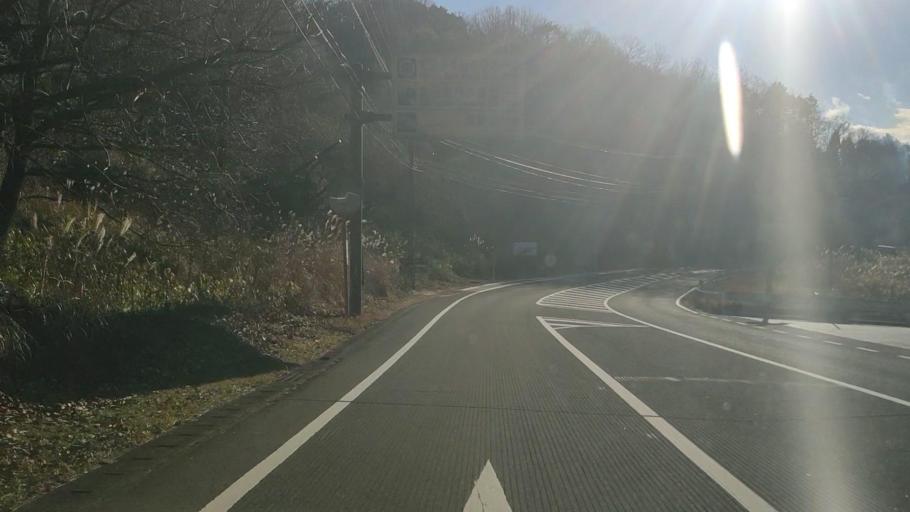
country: JP
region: Saga Prefecture
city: Kanzakimachi-kanzaki
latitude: 33.4118
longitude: 130.2749
